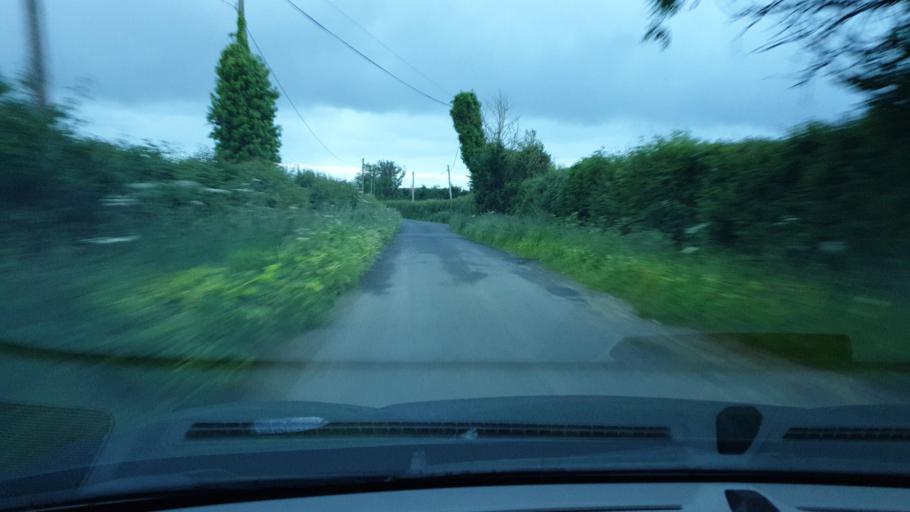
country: IE
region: Leinster
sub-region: An Mhi
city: Ashbourne
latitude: 53.5121
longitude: -6.3583
